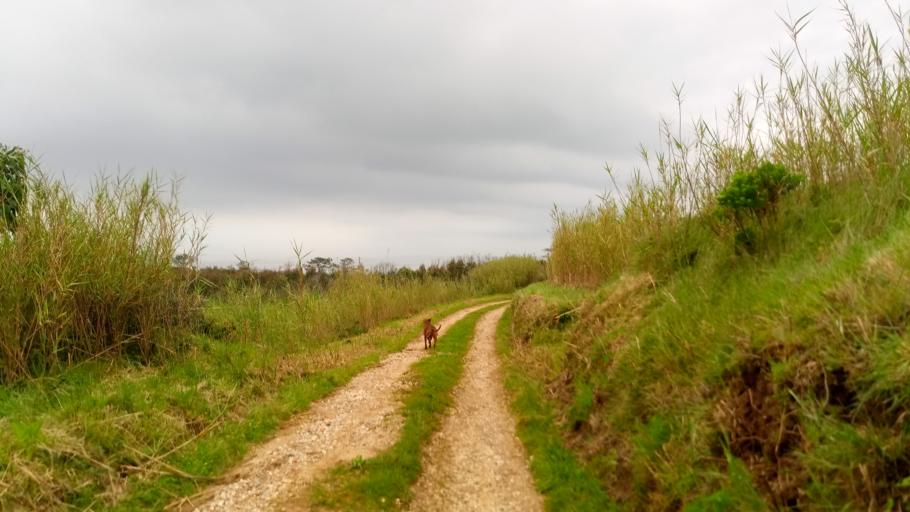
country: PT
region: Leiria
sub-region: Caldas da Rainha
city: Caldas da Rainha
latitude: 39.4681
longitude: -9.1979
